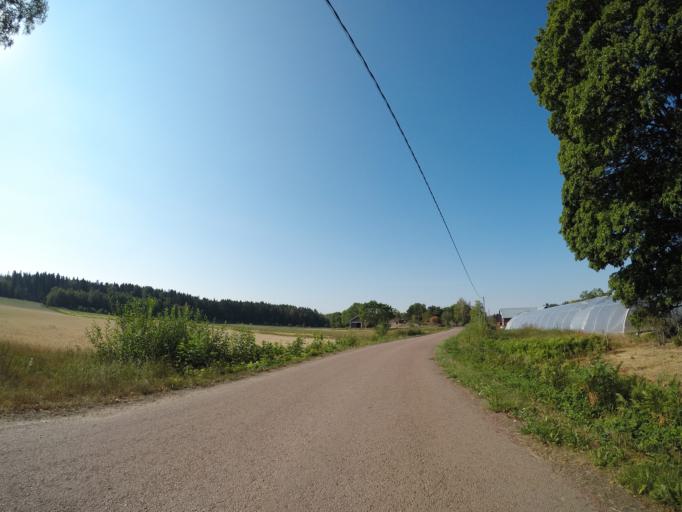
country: AX
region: Alands landsbygd
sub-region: Finstroem
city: Finstroem
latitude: 60.2714
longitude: 19.9399
